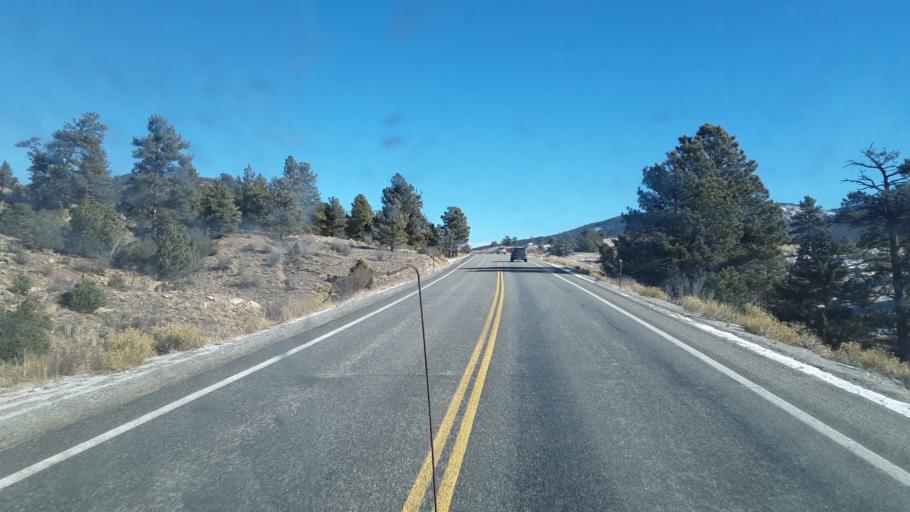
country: US
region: Colorado
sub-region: Chaffee County
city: Buena Vista
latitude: 38.8423
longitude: -105.9941
